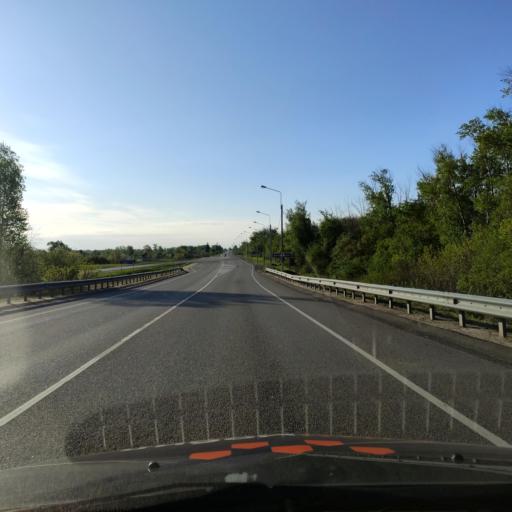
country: RU
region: Lipetsk
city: Yelets
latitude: 52.5616
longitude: 38.6844
